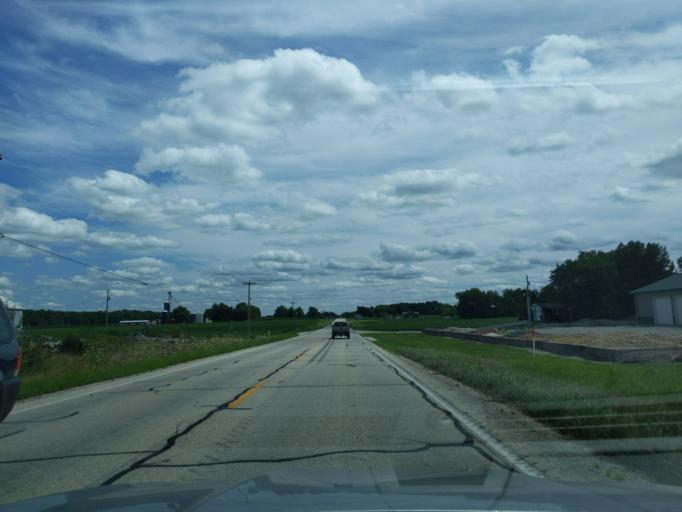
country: US
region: Indiana
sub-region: Ripley County
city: Batesville
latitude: 39.3085
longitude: -85.2787
